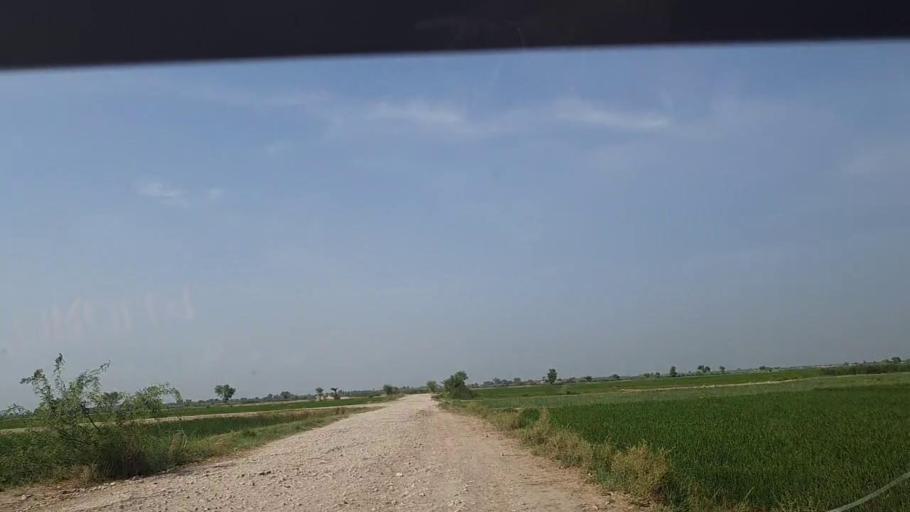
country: PK
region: Sindh
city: Khanpur
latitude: 27.8474
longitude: 69.3774
